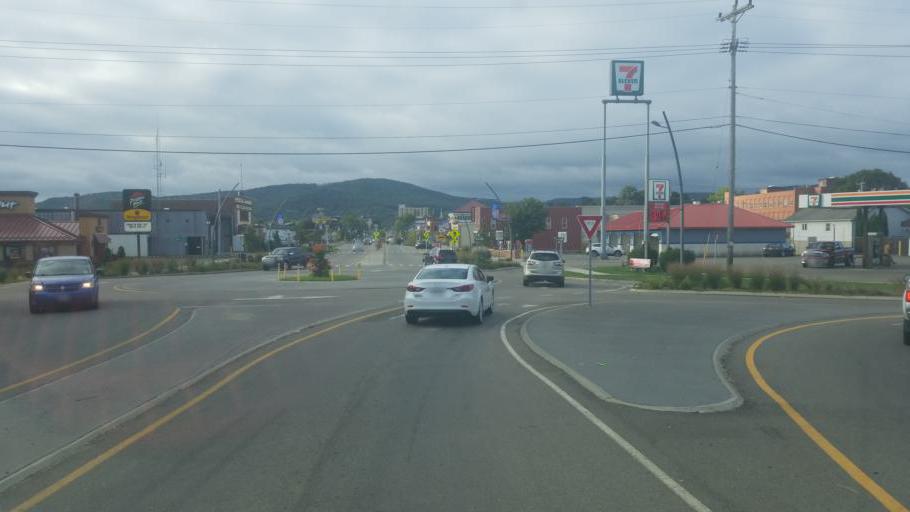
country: US
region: New York
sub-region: Cattaraugus County
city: Olean
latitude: 42.0874
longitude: -78.4300
